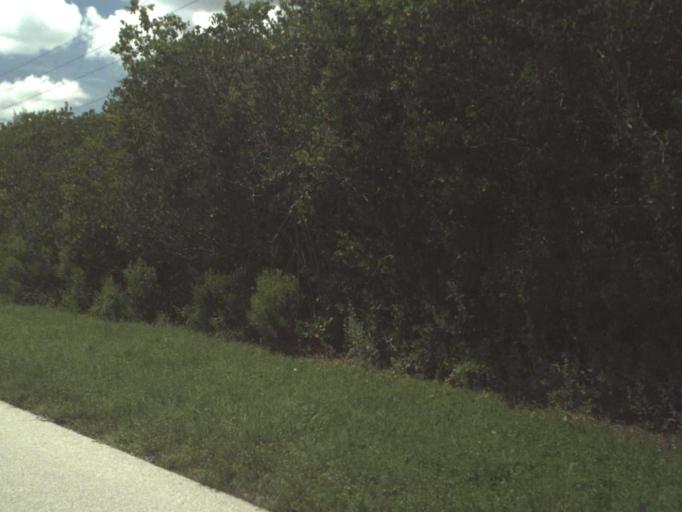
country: US
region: Florida
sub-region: Saint Lucie County
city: Indian River Estates
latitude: 27.3742
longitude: -80.2537
